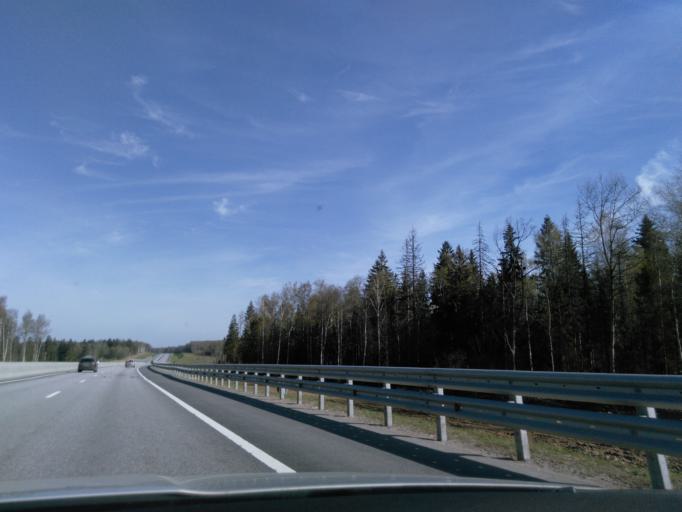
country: RU
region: Moskovskaya
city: Lozhki
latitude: 56.1174
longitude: 37.1168
